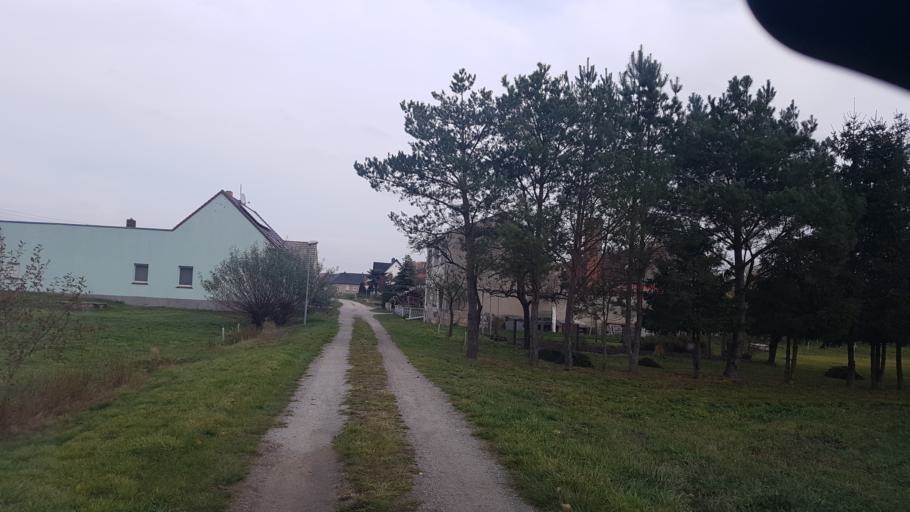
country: DE
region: Brandenburg
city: Schilda
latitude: 51.6443
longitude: 13.3836
